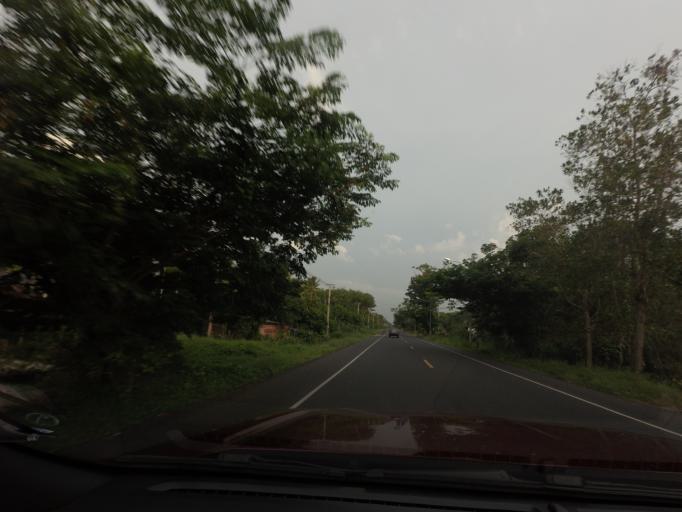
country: TH
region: Pattani
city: Mae Lan
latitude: 6.6157
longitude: 101.1901
